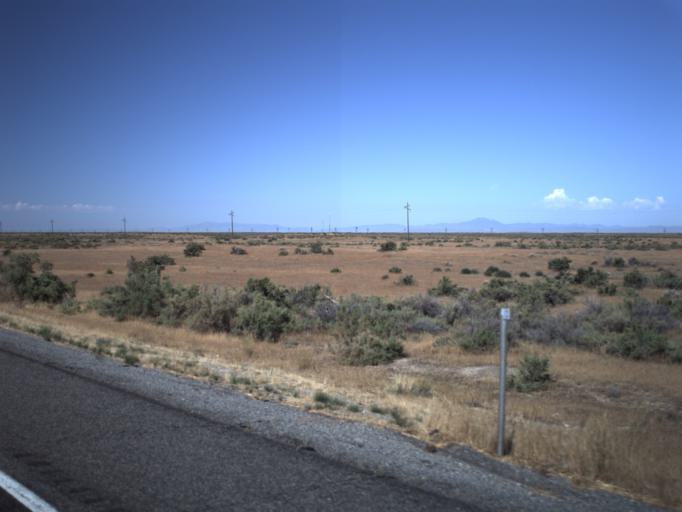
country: US
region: Utah
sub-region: Millard County
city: Delta
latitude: 39.4459
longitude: -112.4502
